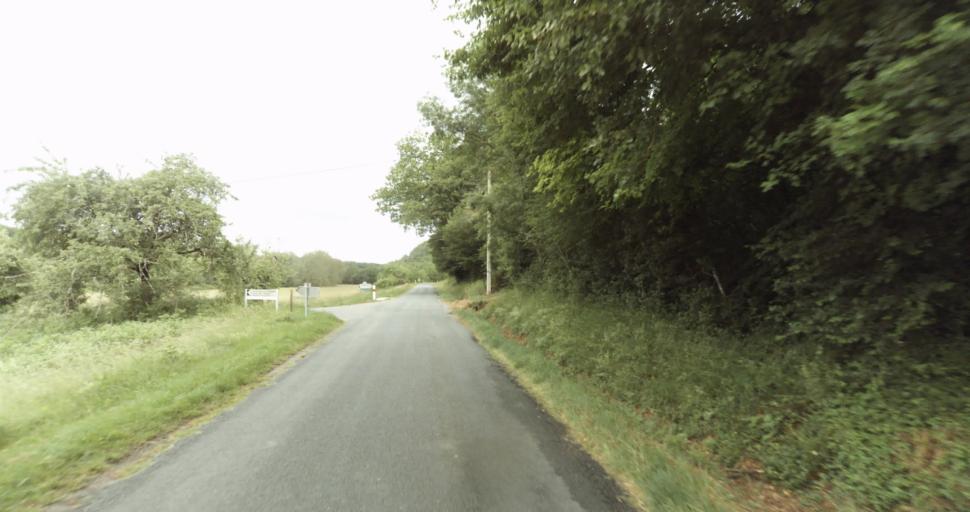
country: FR
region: Aquitaine
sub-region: Departement de la Dordogne
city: Beaumont-du-Perigord
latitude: 44.7525
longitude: 0.8253
